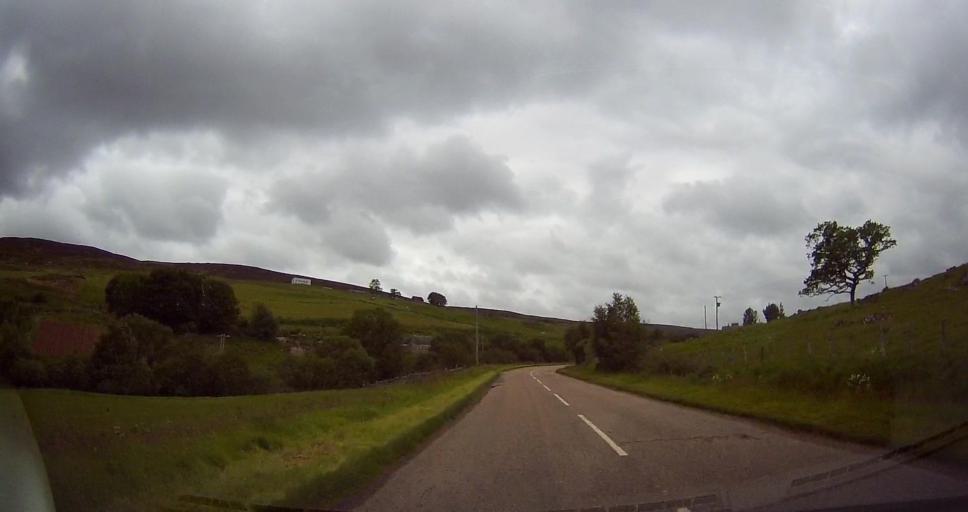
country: GB
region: Scotland
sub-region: Highland
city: Dornoch
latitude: 58.0058
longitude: -4.2145
